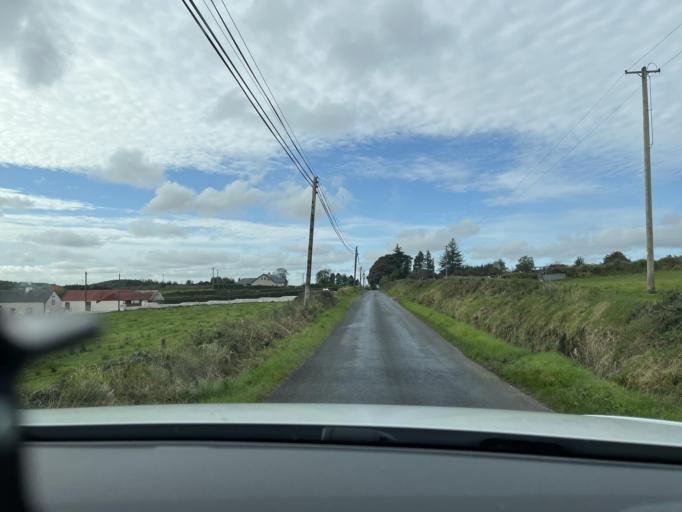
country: IE
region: Connaught
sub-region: Roscommon
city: Boyle
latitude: 54.0188
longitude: -8.3756
